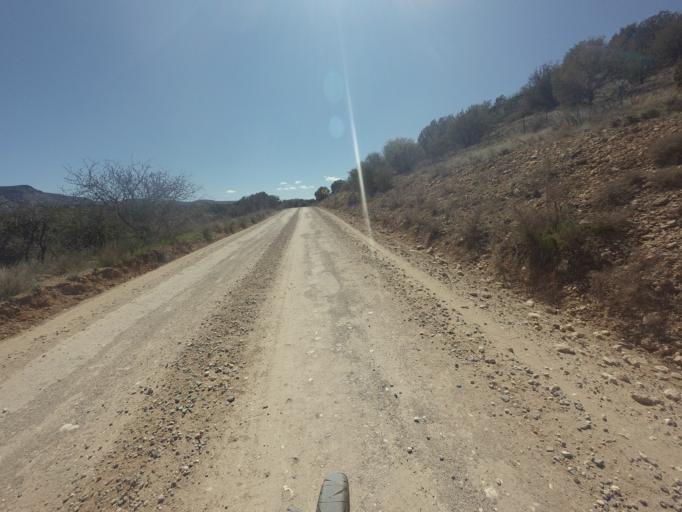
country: US
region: Arizona
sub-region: Yavapai County
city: Lake Montezuma
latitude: 34.6391
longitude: -111.7185
